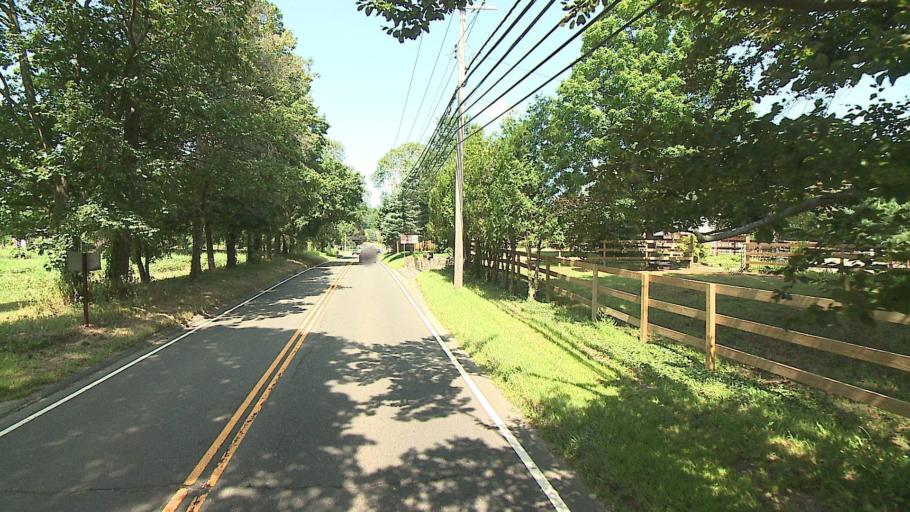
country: US
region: Connecticut
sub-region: Fairfield County
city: Trumbull
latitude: 41.2474
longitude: -73.2769
